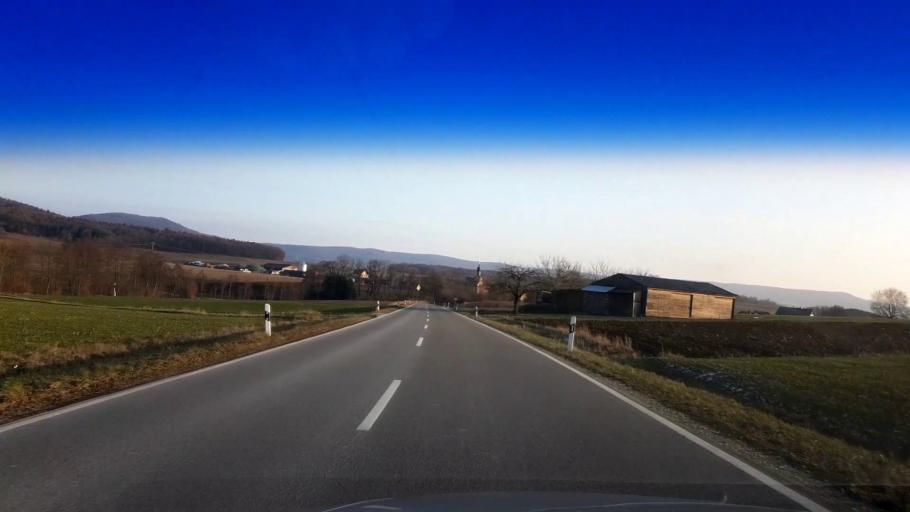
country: DE
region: Bavaria
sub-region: Upper Franconia
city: Schesslitz
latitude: 50.0080
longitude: 11.0134
